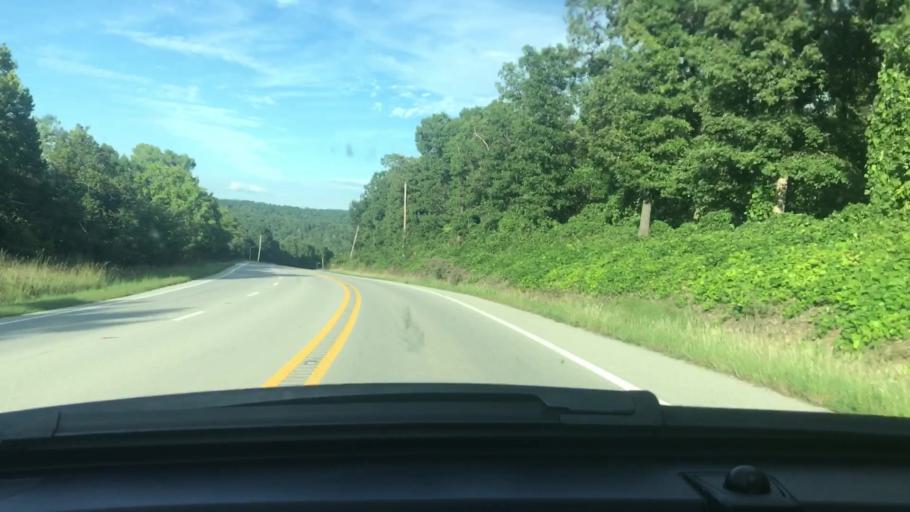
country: US
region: Arkansas
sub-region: Sharp County
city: Cherokee Village
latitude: 36.2721
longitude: -91.3673
